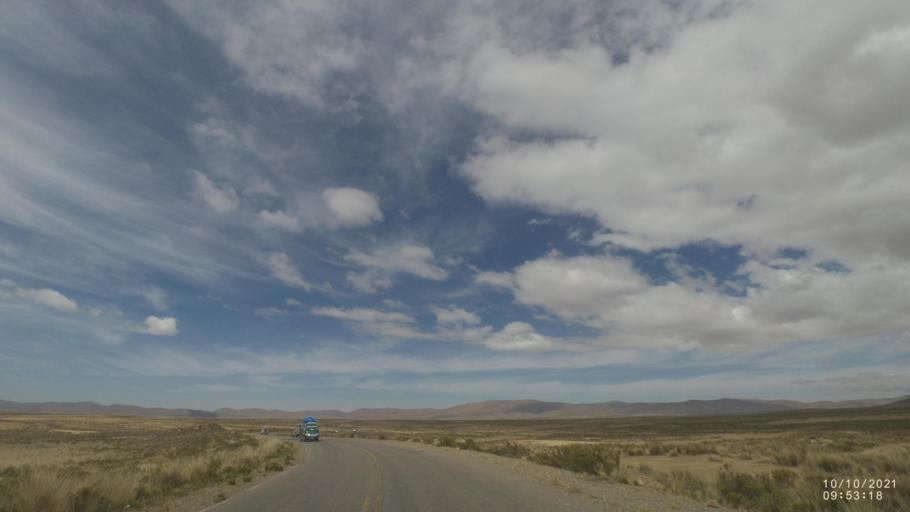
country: BO
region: La Paz
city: Colquiri
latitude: -17.2792
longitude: -67.3491
